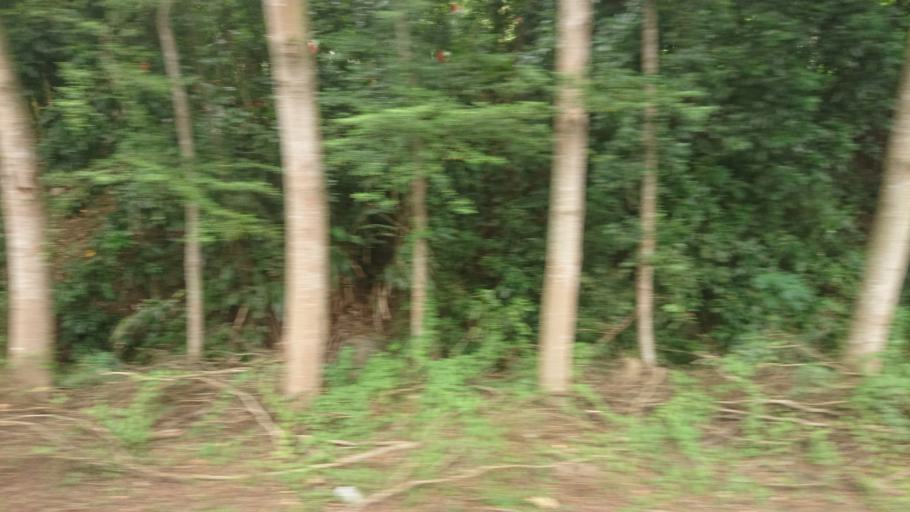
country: TW
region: Taiwan
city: Lugu
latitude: 23.8184
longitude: 120.8525
